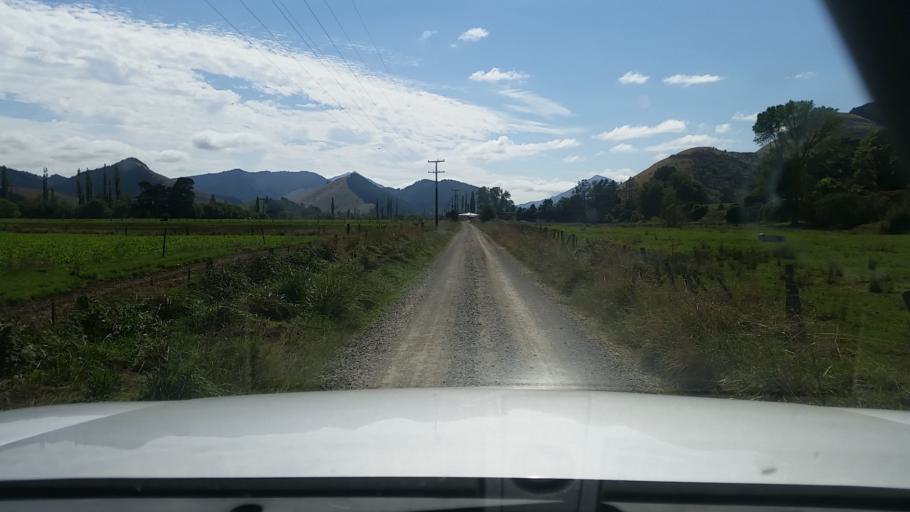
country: NZ
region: Nelson
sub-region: Nelson City
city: Nelson
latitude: -41.2527
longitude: 173.5826
